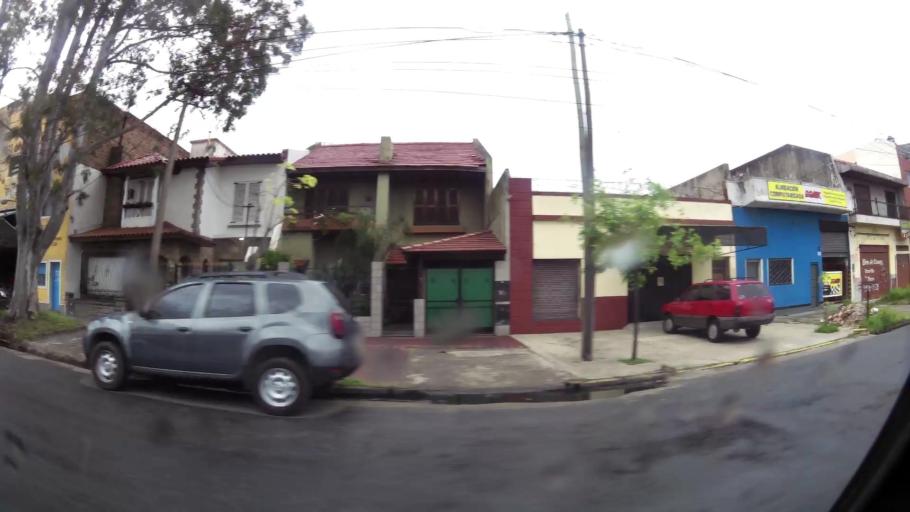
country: AR
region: Buenos Aires
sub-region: Partido de Lanus
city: Lanus
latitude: -34.6819
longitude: -58.4048
